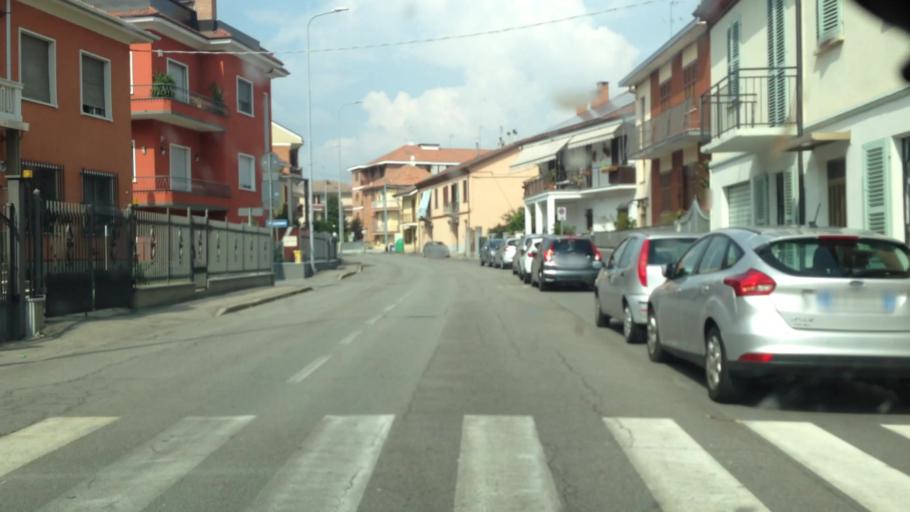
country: IT
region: Piedmont
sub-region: Provincia di Asti
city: Asti
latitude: 44.9065
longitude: 8.2126
